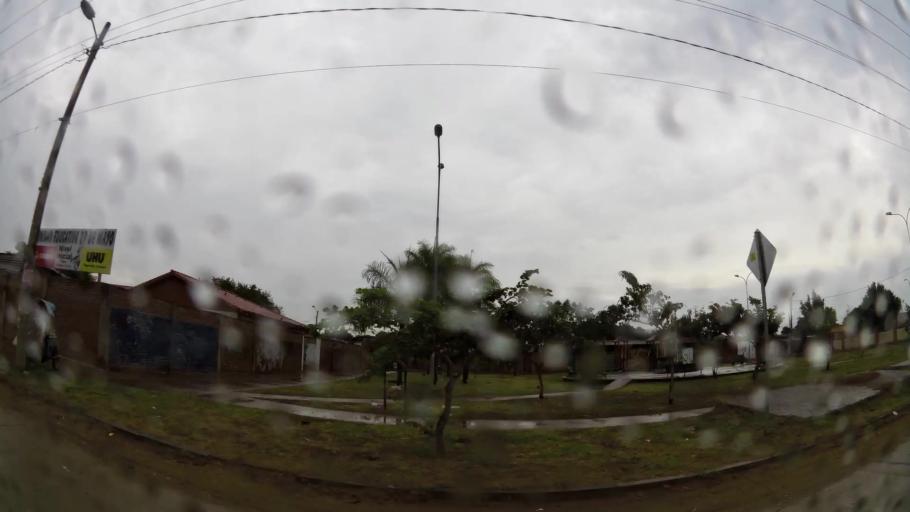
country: BO
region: Santa Cruz
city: Santa Cruz de la Sierra
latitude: -17.8022
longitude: -63.1291
